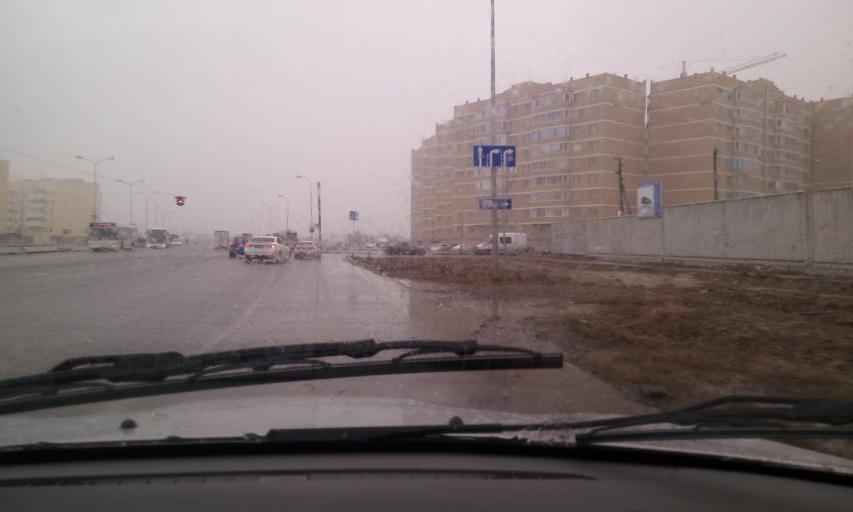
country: KZ
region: Astana Qalasy
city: Astana
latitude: 51.1719
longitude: 71.3740
